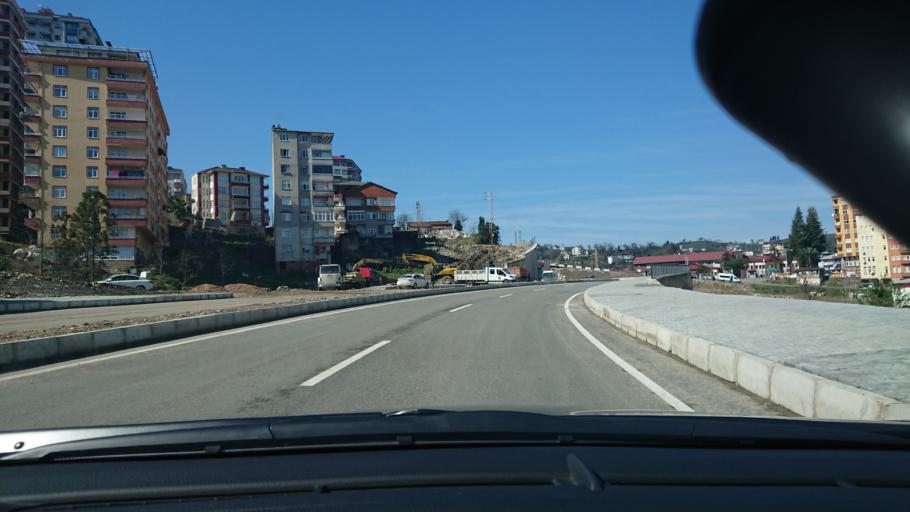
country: TR
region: Rize
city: Rize
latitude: 41.0149
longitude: 40.5137
